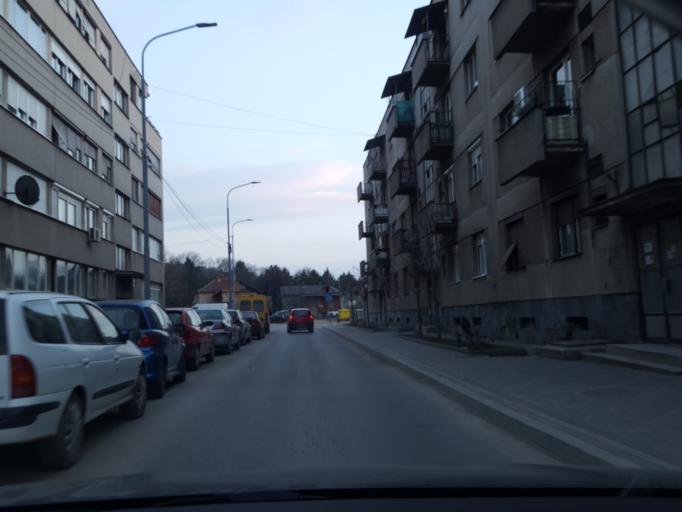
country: RS
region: Central Serbia
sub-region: Nisavski Okrug
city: Aleksinac
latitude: 43.5372
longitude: 21.7091
